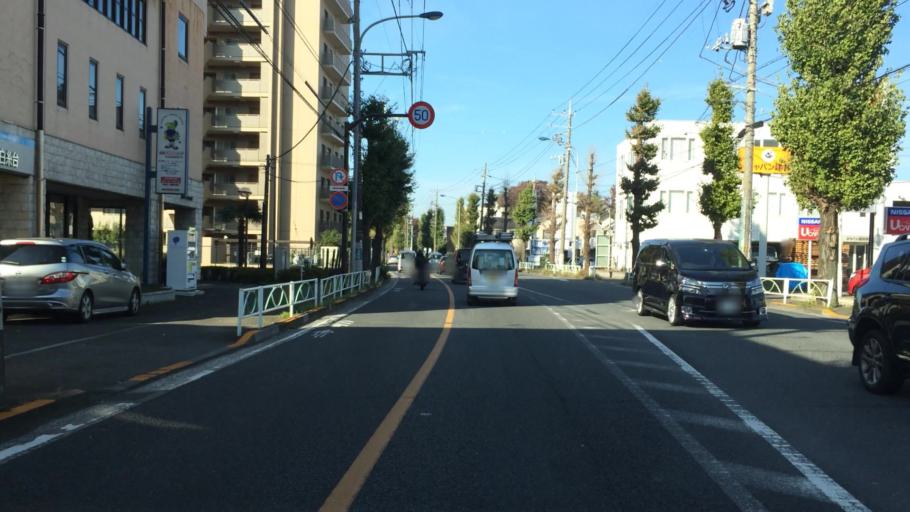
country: JP
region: Tokyo
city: Chofugaoka
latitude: 35.6700
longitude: 139.5082
